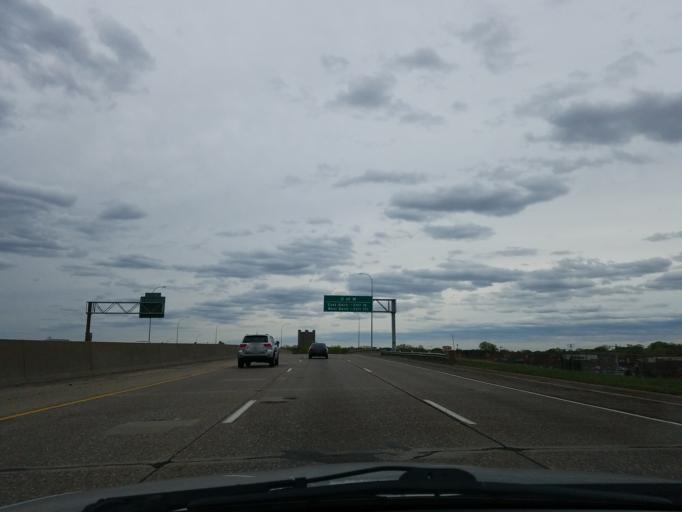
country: US
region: Minnesota
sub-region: Hennepin County
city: Saint Anthony
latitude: 45.0018
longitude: -93.2282
